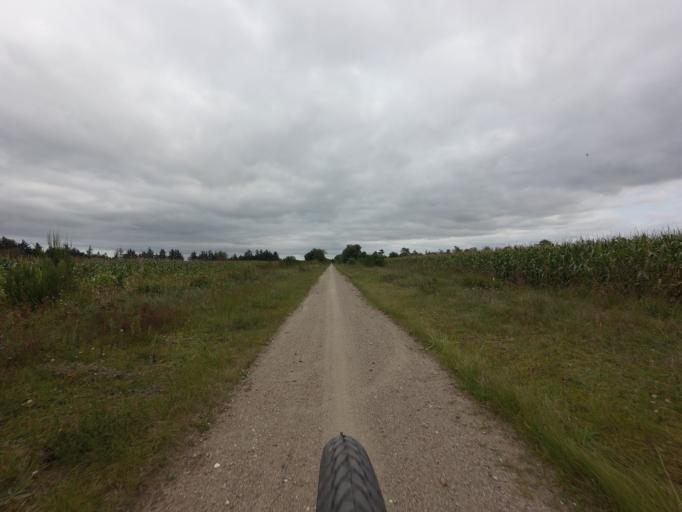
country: DK
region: South Denmark
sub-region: Billund Kommune
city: Grindsted
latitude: 55.7883
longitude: 8.9642
